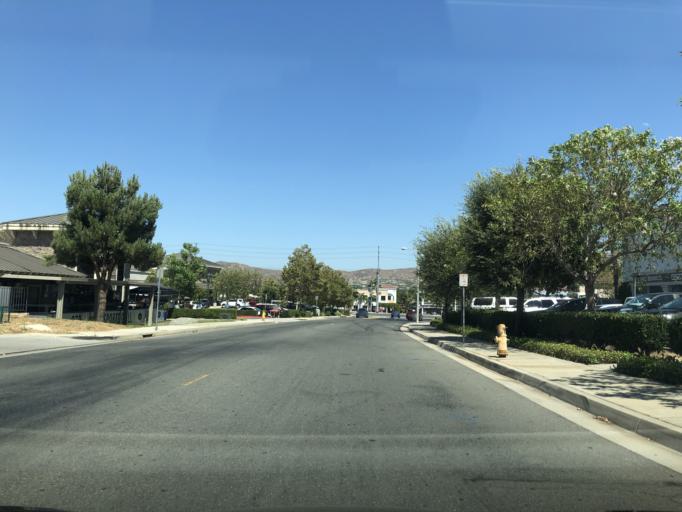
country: US
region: California
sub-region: Riverside County
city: Norco
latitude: 33.9282
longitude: -117.5600
